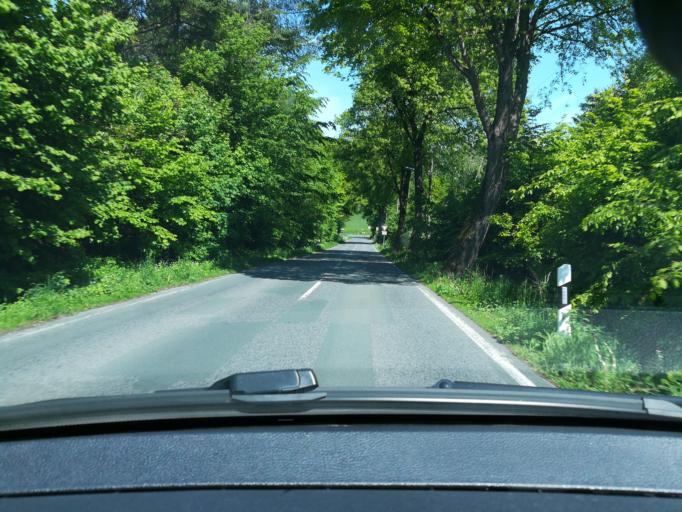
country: DE
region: North Rhine-Westphalia
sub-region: Regierungsbezirk Detmold
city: Oerlinghausen
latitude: 51.9755
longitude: 8.6211
